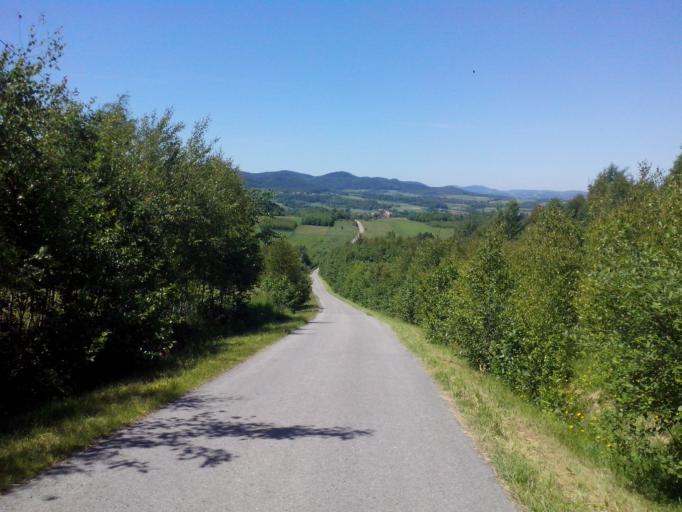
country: PL
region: Subcarpathian Voivodeship
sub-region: Powiat strzyzowski
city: Wysoka Strzyzowska
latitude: 49.8186
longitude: 21.7655
